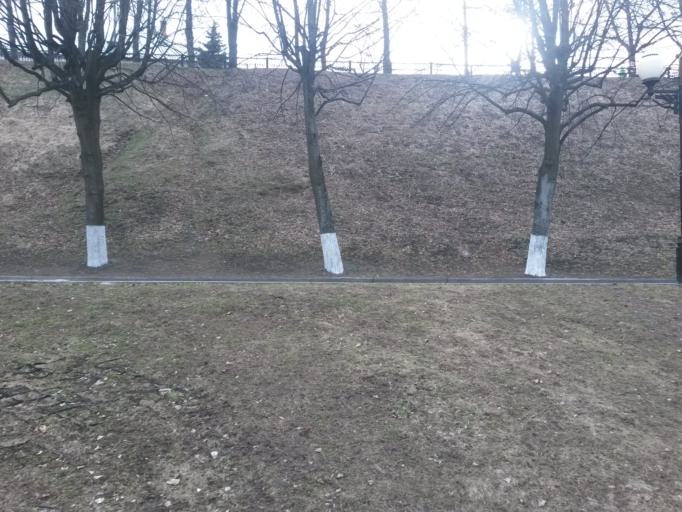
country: RU
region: Jaroslavl
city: Yaroslavl
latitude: 57.6239
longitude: 39.9034
